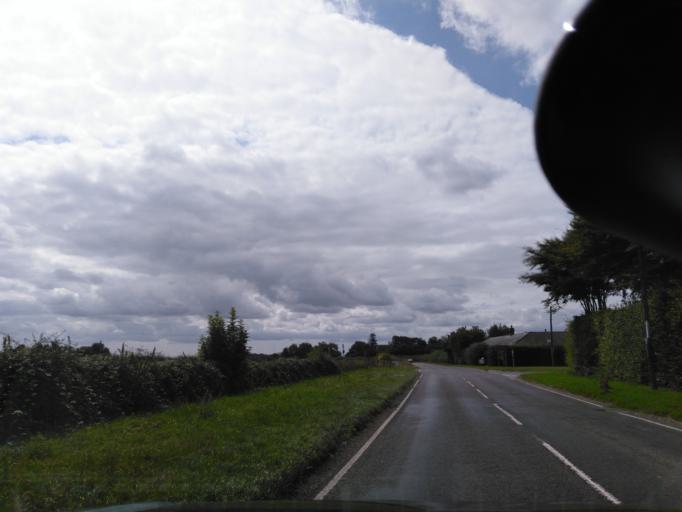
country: GB
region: England
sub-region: Dorset
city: Blandford Forum
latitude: 50.9302
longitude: -2.1640
